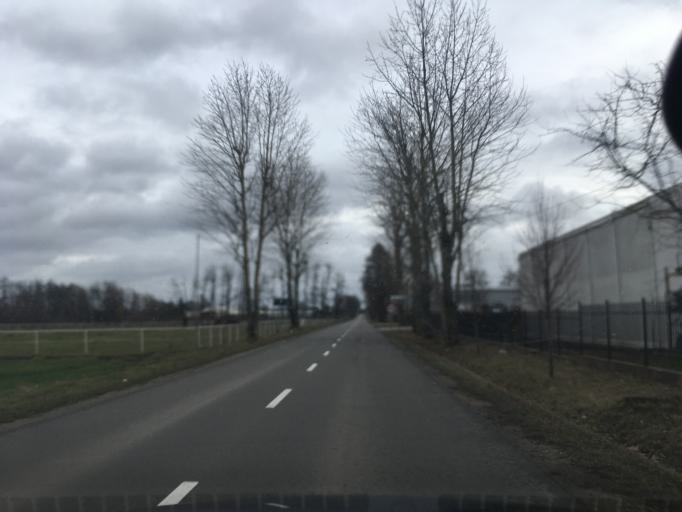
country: PL
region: Masovian Voivodeship
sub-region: Powiat piaseczynski
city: Lesznowola
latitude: 52.1212
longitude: 20.9350
